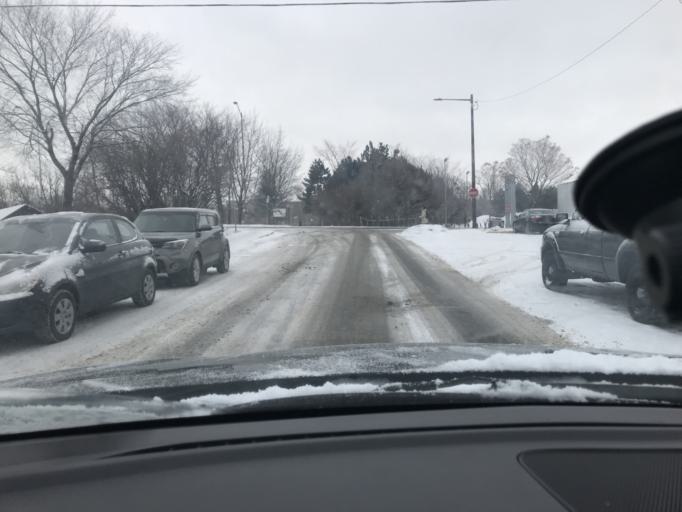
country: CA
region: Quebec
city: Quebec
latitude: 46.8202
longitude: -71.2235
